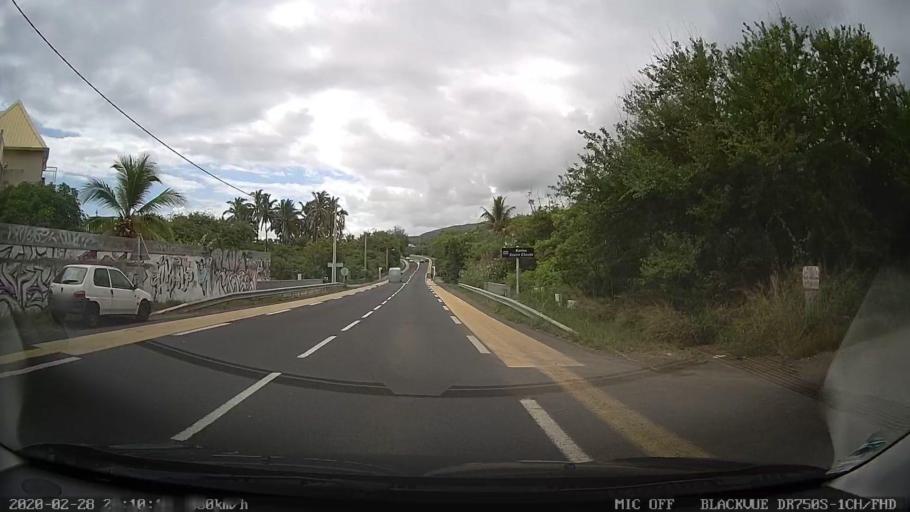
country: RE
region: Reunion
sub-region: Reunion
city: Trois-Bassins
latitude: -21.1210
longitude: 55.2610
